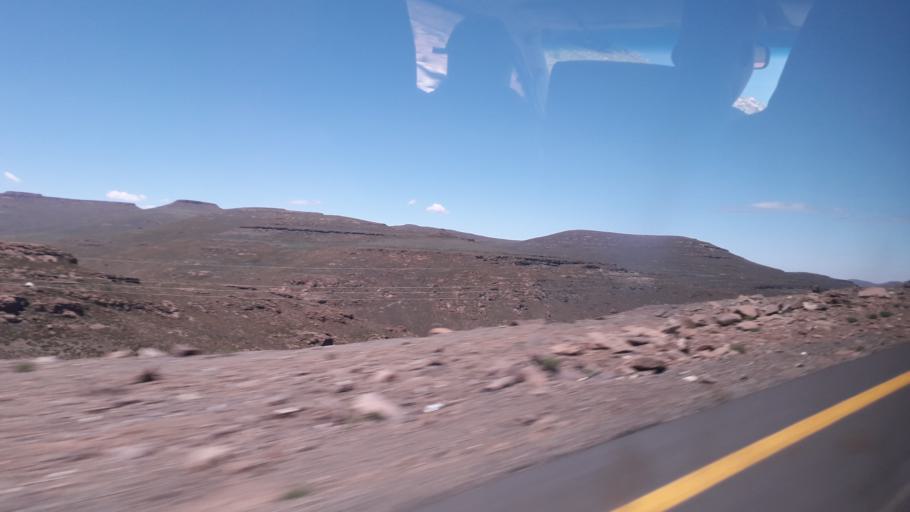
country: ZA
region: Orange Free State
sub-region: Thabo Mofutsanyana District Municipality
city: Phuthaditjhaba
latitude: -28.8290
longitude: 28.7364
